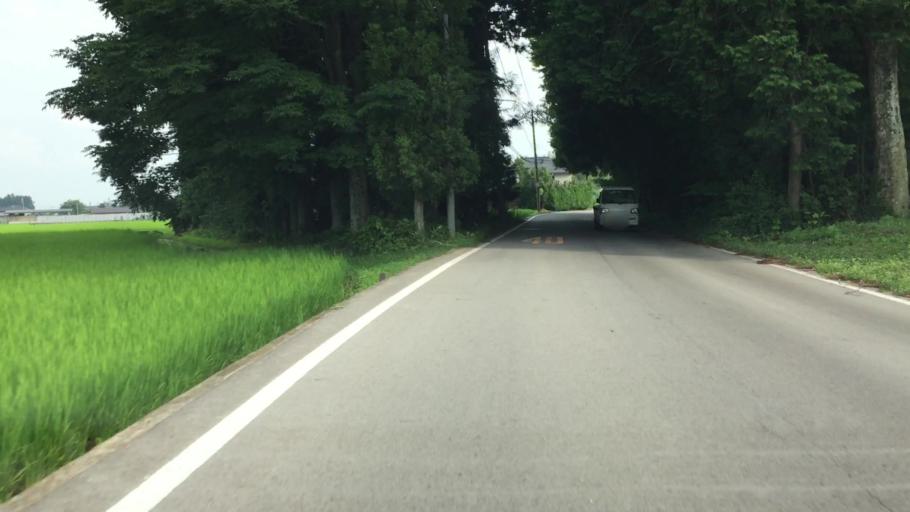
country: JP
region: Tochigi
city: Kuroiso
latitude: 36.9646
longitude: 139.9806
